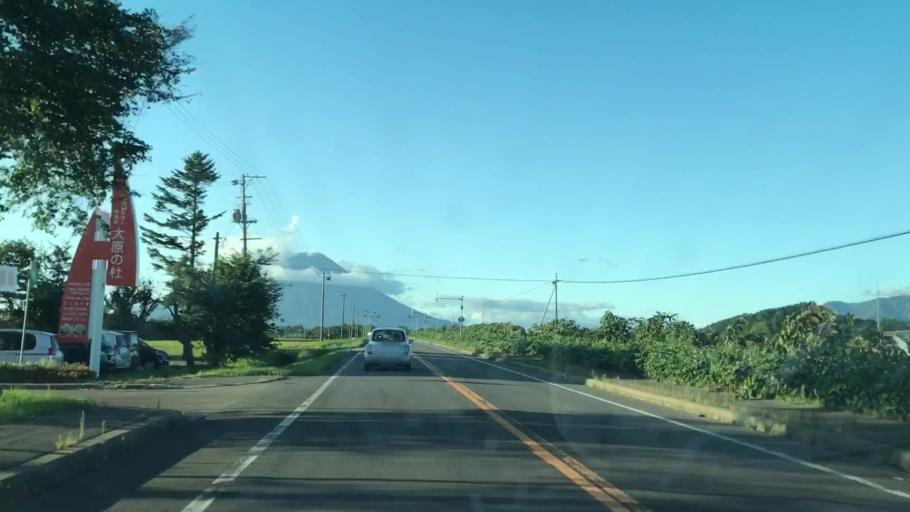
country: JP
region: Hokkaido
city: Niseko Town
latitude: 42.6749
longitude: 140.8420
